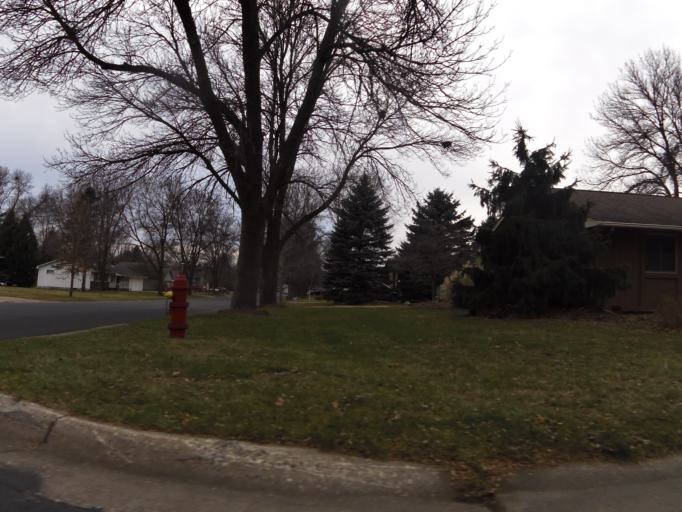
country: US
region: Wisconsin
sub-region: Pierce County
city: River Falls
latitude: 44.8570
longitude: -92.6107
